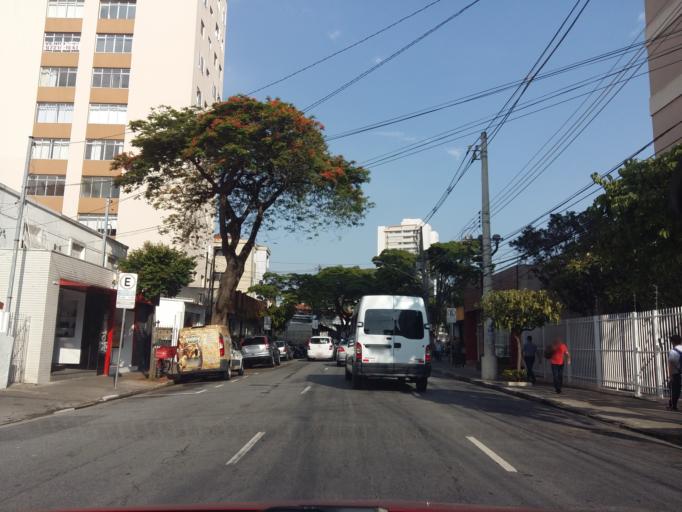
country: BR
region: Sao Paulo
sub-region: Sao Paulo
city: Sao Paulo
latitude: -23.6057
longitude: -46.6927
